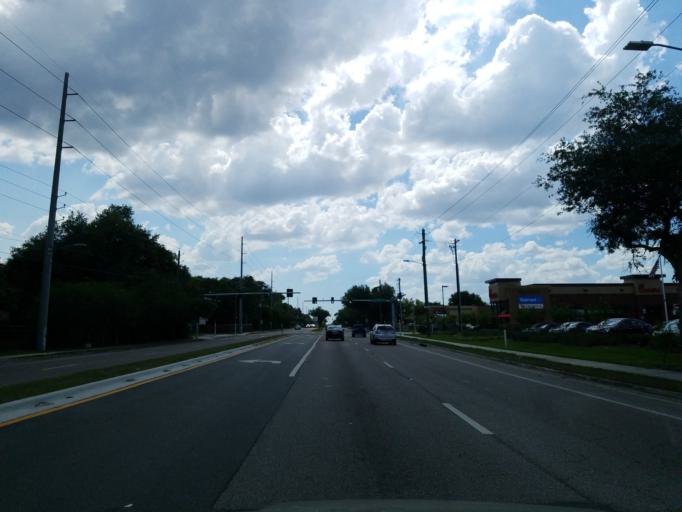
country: US
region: Florida
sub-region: Hillsborough County
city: Bloomingdale
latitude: 27.8937
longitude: -82.2502
